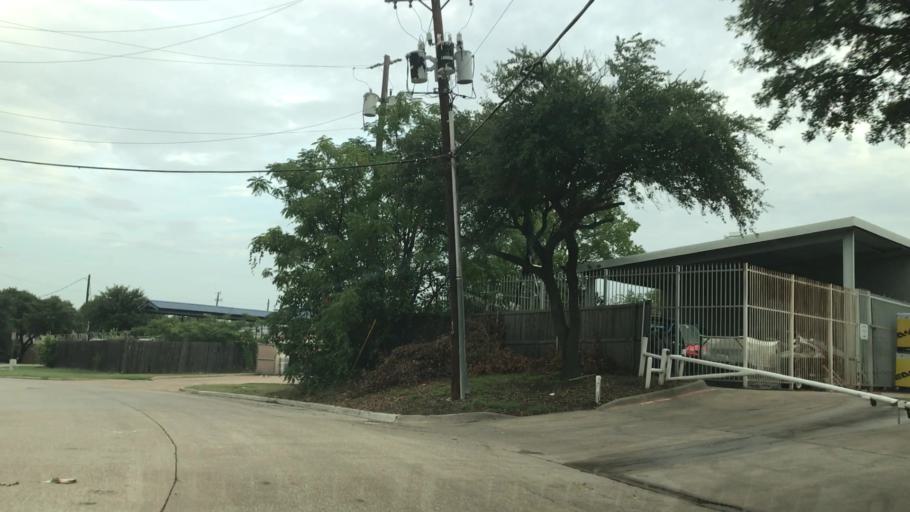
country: US
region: Texas
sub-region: Dallas County
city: Garland
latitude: 32.8839
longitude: -96.6994
